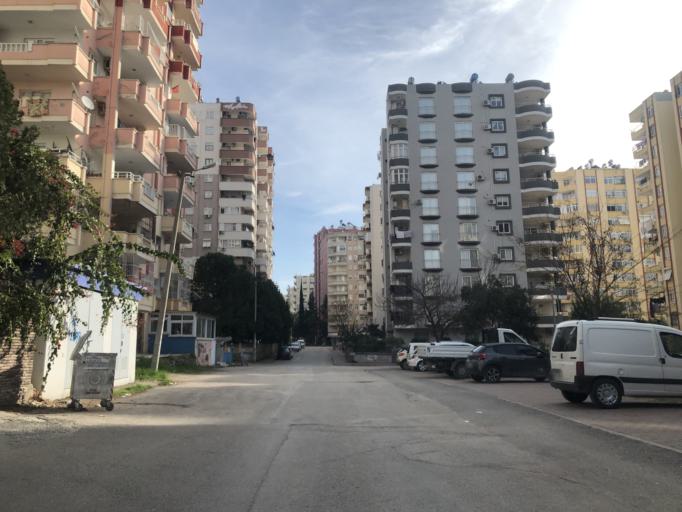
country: TR
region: Adana
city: Adana
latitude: 37.0518
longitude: 35.2886
